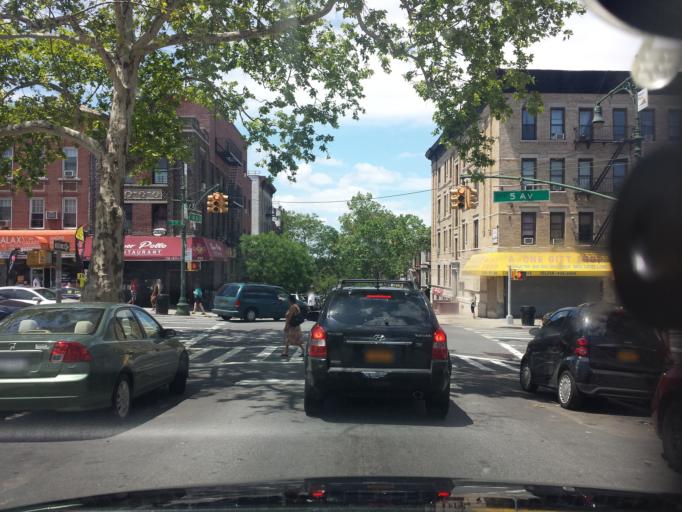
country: US
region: New York
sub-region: Kings County
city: Bensonhurst
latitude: 40.6500
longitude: -74.0049
